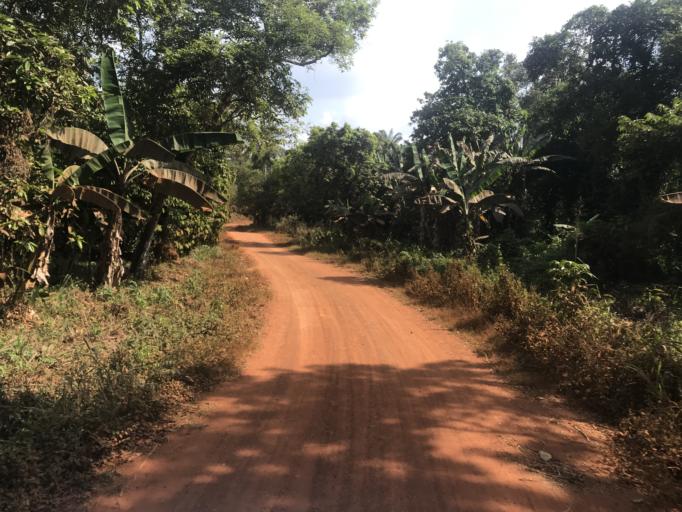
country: NG
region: Osun
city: Ibokun
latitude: 7.8015
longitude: 4.6870
